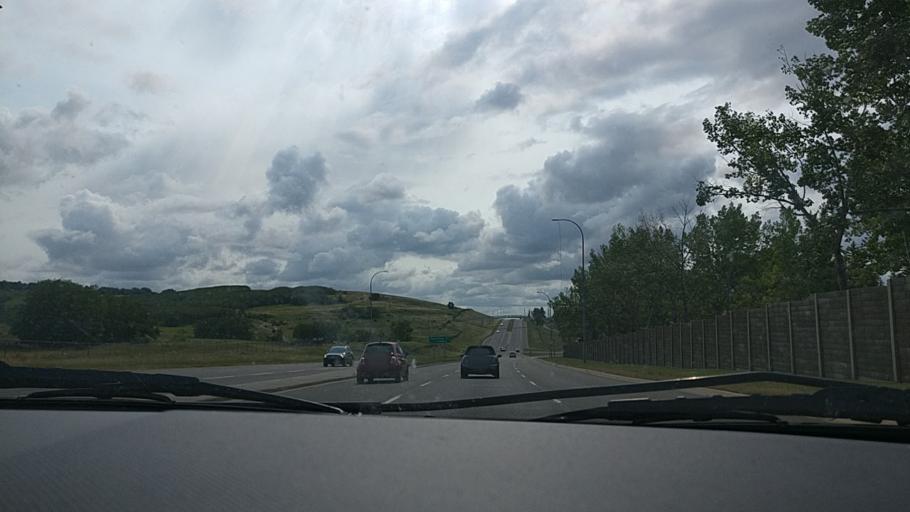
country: CA
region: Alberta
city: Calgary
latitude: 51.1052
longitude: -114.1313
